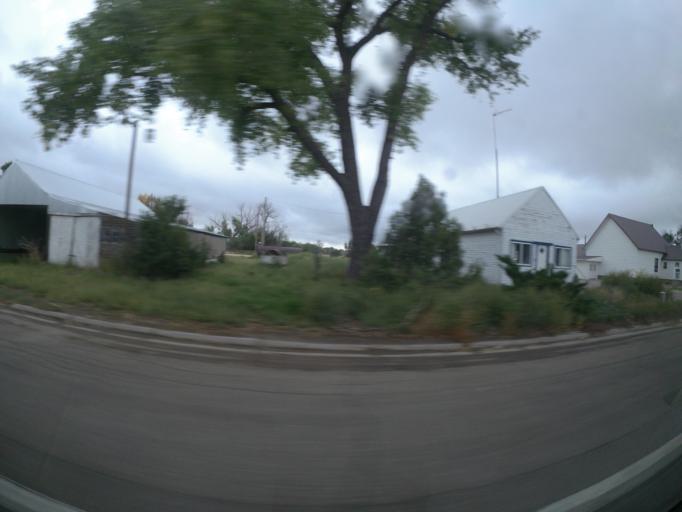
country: US
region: Colorado
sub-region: Yuma County
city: Yuma
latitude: 39.6631
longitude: -102.8510
